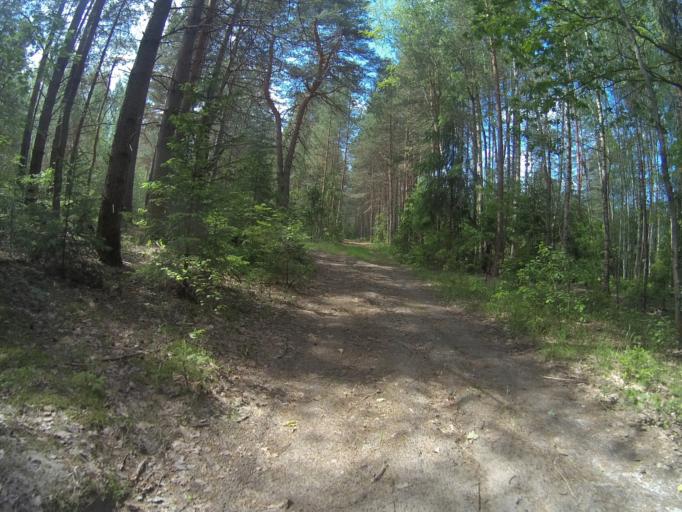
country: RU
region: Vladimir
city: Raduzhnyy
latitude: 56.0266
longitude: 40.2678
